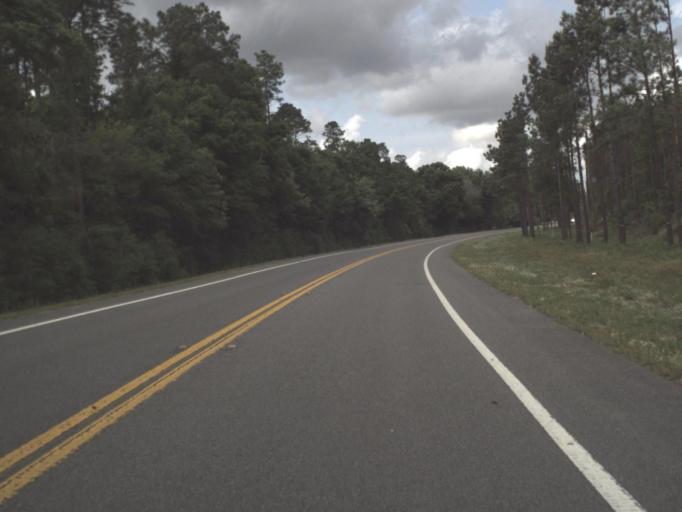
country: US
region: Florida
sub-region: Santa Rosa County
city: Point Baker
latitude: 30.7348
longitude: -87.0927
